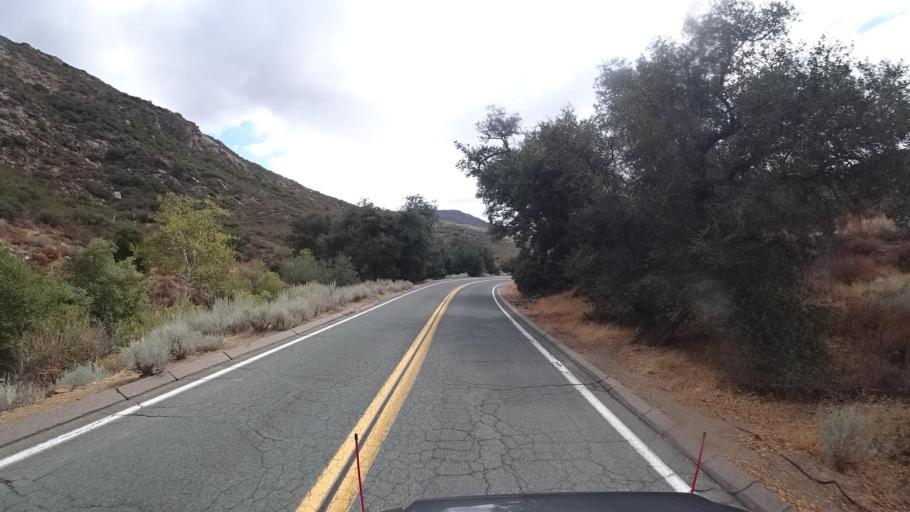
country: US
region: California
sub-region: San Diego County
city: Pine Valley
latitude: 32.7699
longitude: -116.4507
